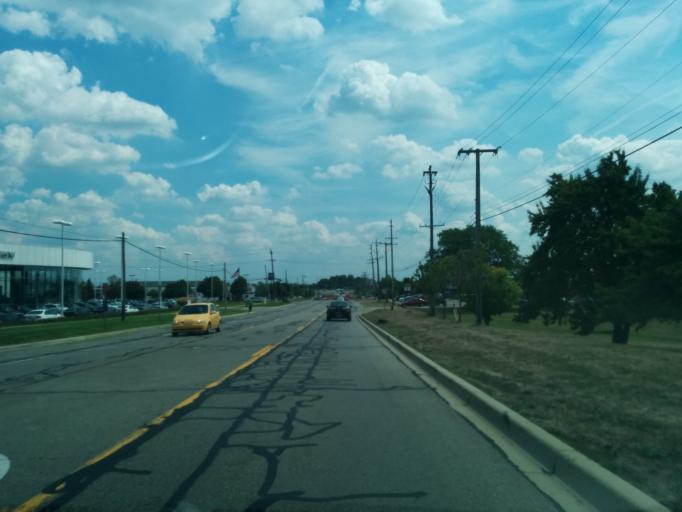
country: US
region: Michigan
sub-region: Oakland County
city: Novi
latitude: 42.4700
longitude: -83.4278
